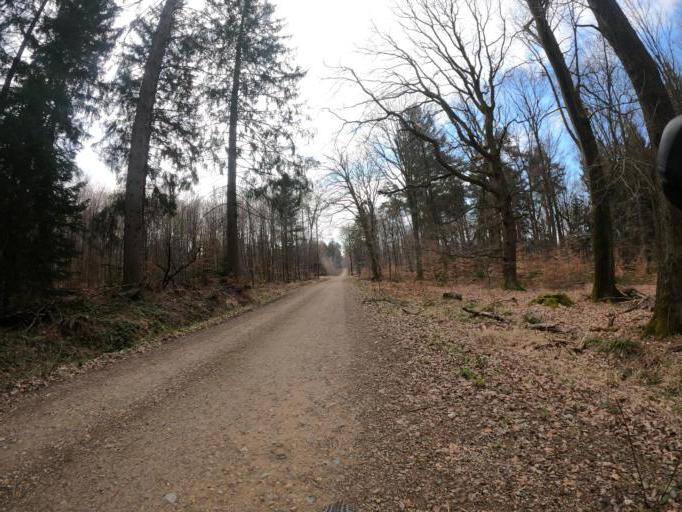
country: DE
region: North Rhine-Westphalia
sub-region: Regierungsbezirk Koln
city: Roetgen
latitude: 50.6711
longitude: 6.1741
